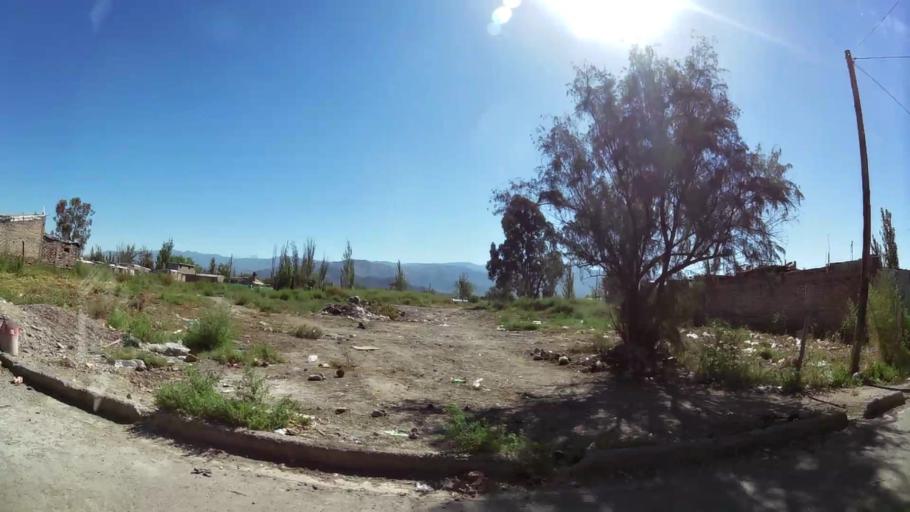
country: AR
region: Mendoza
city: Las Heras
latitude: -32.8265
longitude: -68.8168
